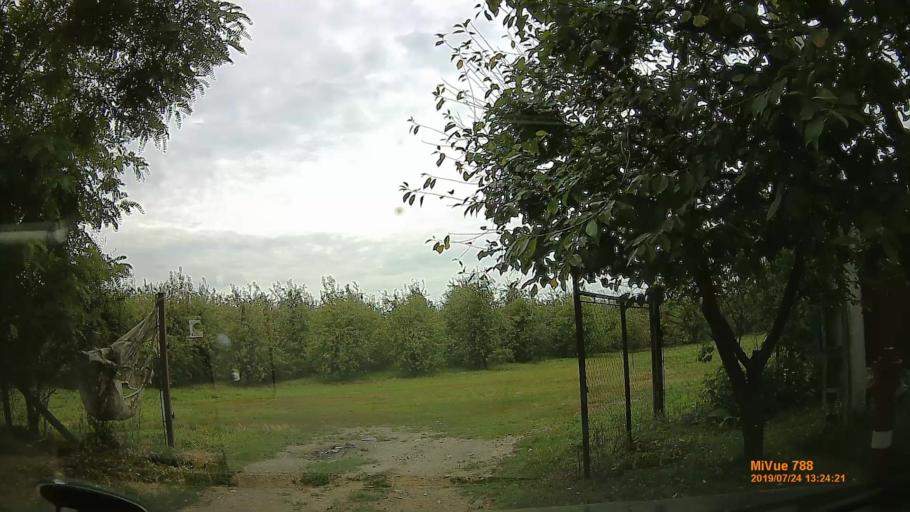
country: UA
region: Zakarpattia
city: Batiovo
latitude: 48.2248
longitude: 22.4159
